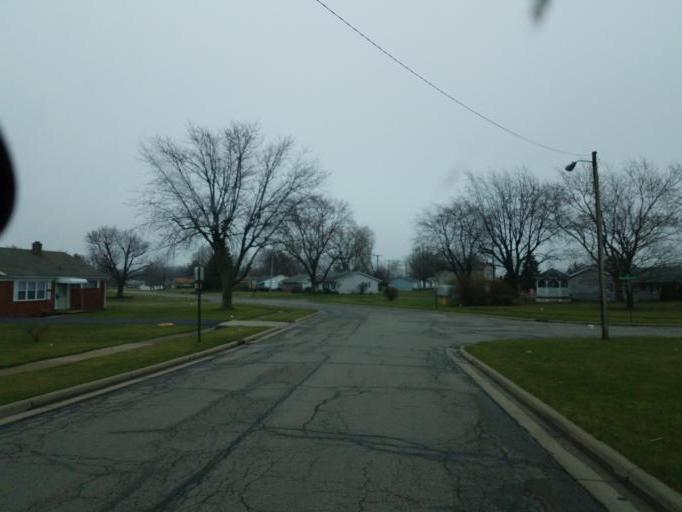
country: US
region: Ohio
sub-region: Richland County
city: Ontario
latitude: 40.7736
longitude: -82.5889
